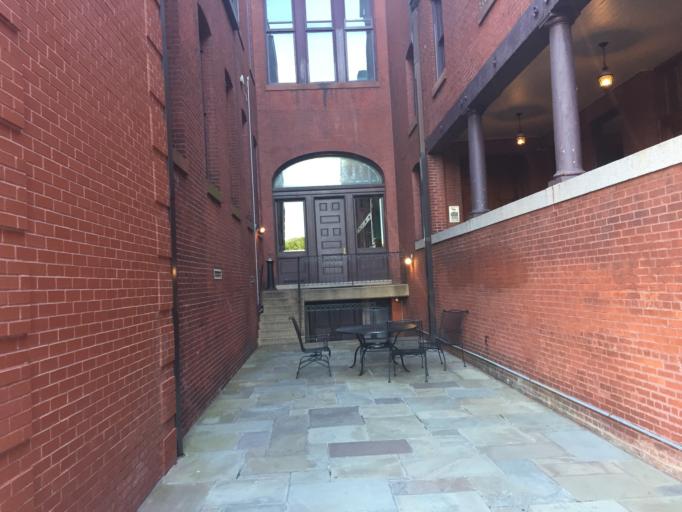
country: US
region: Maryland
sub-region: City of Baltimore
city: Baltimore
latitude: 39.3284
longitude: -76.6273
